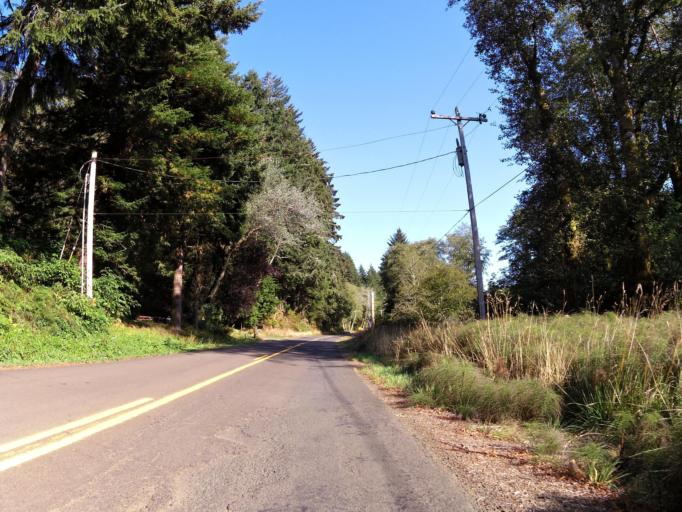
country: US
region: Oregon
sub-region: Lincoln County
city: Rose Lodge
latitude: 45.0749
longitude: -123.9288
